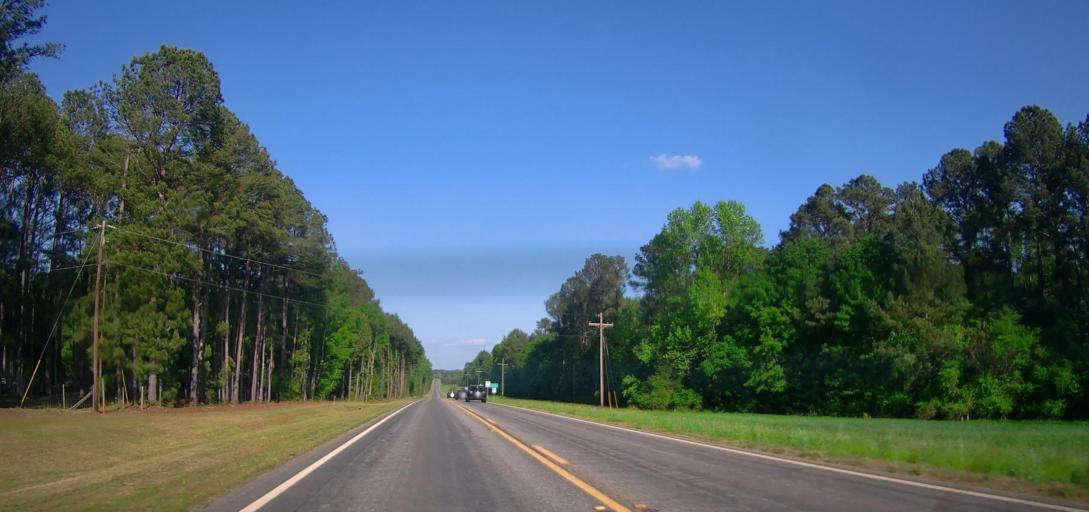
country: US
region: Georgia
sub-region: Walton County
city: Social Circle
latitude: 33.6240
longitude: -83.6314
